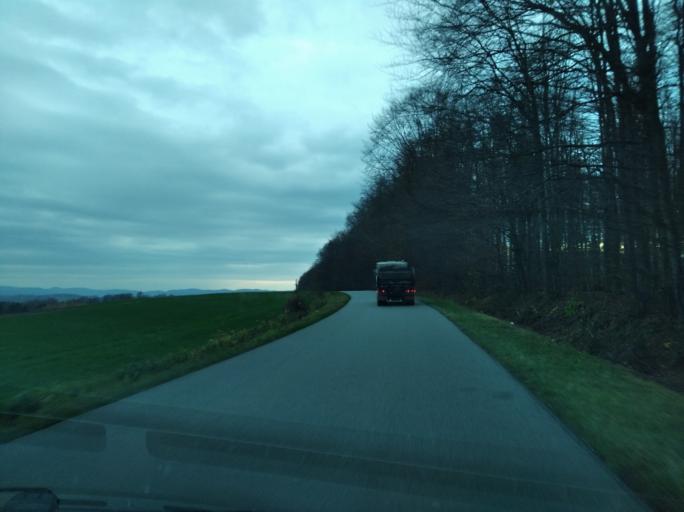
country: PL
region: Subcarpathian Voivodeship
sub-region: Powiat ropczycko-sedziszowski
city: Zagorzyce
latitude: 49.9466
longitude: 21.6943
